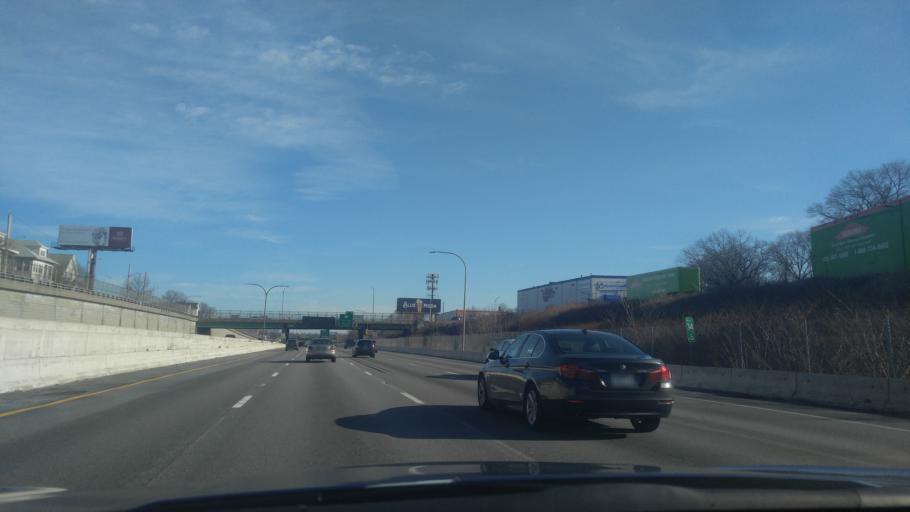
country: US
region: Rhode Island
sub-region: Providence County
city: Cranston
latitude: 41.7942
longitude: -71.4115
